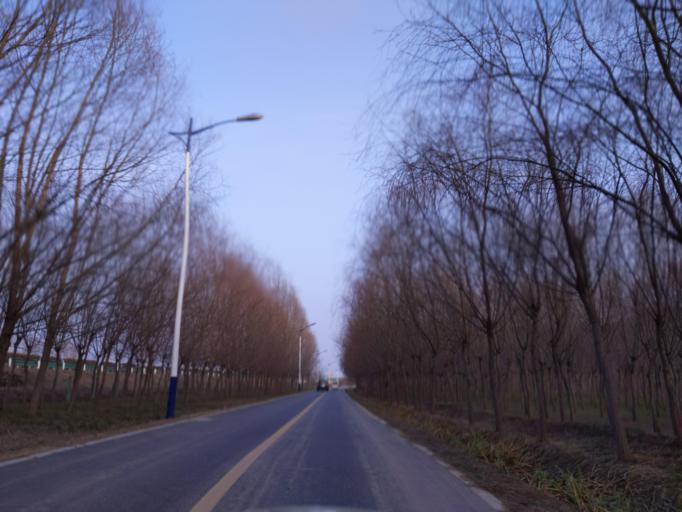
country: CN
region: Henan Sheng
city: Puyang
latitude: 35.8211
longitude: 115.0174
